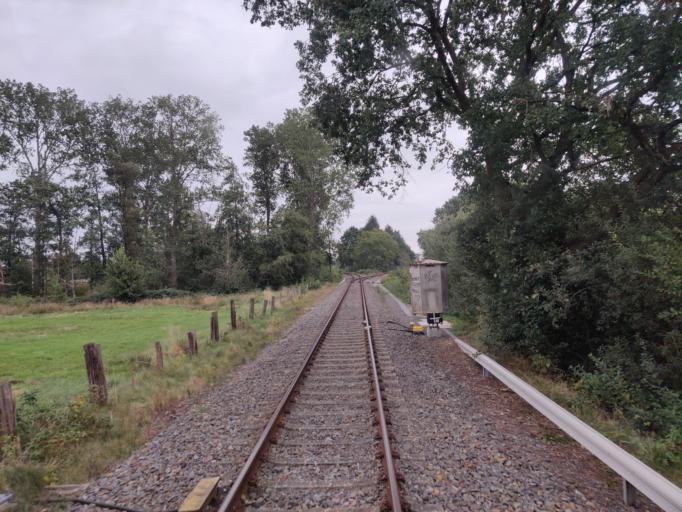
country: DE
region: Lower Saxony
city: Bremervorde
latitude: 53.4863
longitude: 9.1271
